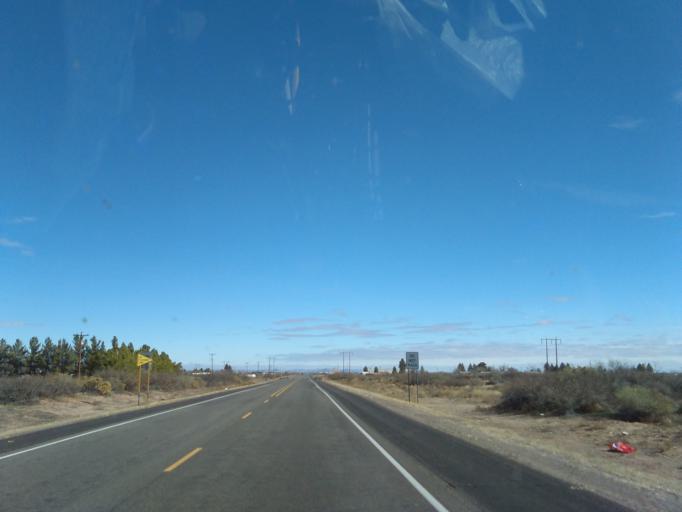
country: US
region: New Mexico
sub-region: Luna County
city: Deming
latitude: 32.2930
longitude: -107.7408
